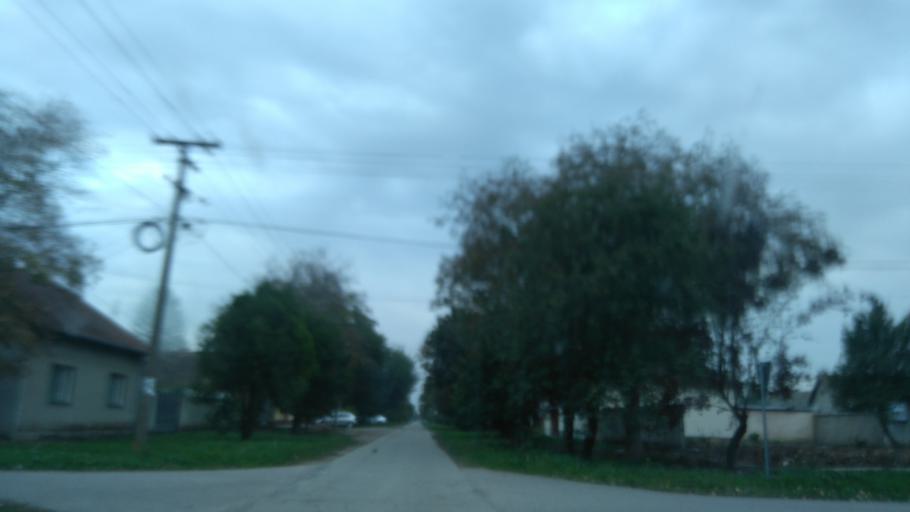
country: RS
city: Mol
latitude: 45.7635
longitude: 20.1407
